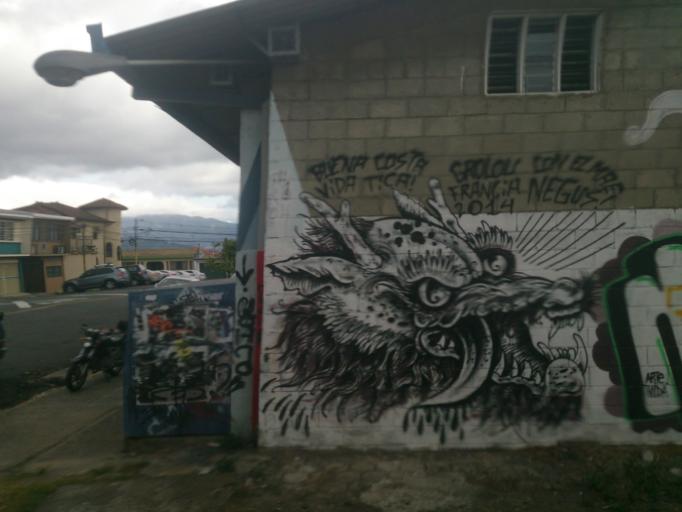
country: CR
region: San Jose
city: San Pedro
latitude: 9.9336
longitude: -84.0657
